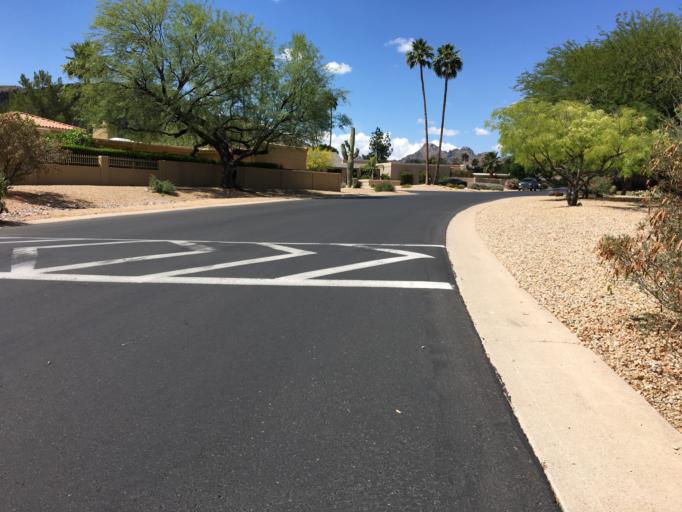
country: US
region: Arizona
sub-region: Maricopa County
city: Paradise Valley
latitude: 33.5763
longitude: -111.9878
